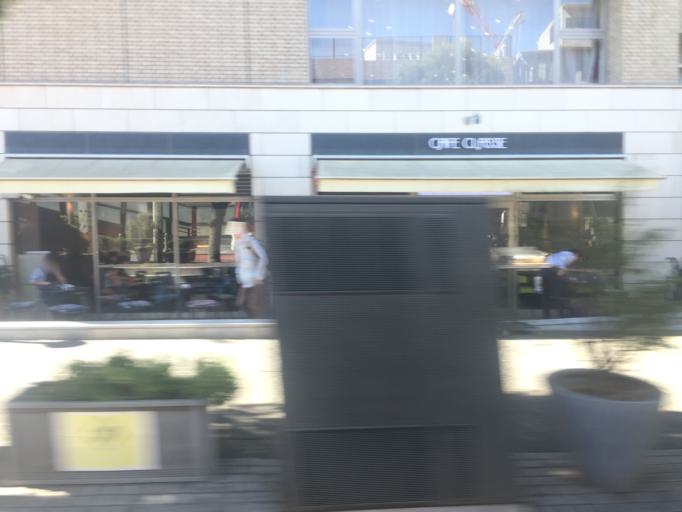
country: JP
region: Tokyo
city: Tokyo
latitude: 35.6491
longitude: 139.7042
